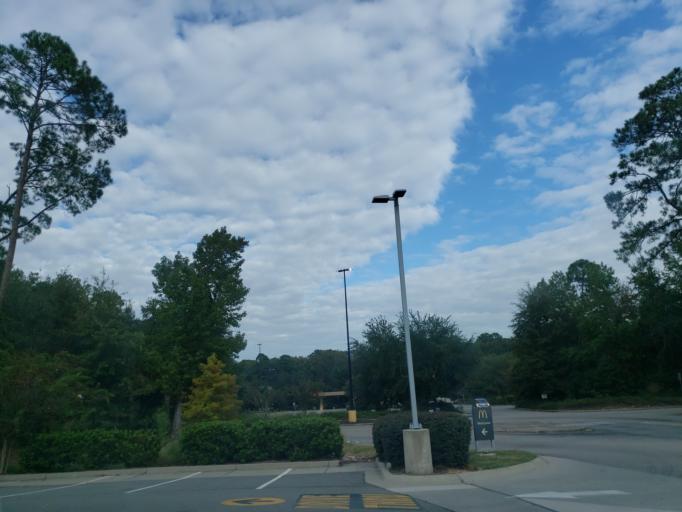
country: US
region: Georgia
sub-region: Chatham County
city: Isle of Hope
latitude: 31.9890
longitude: -81.0814
